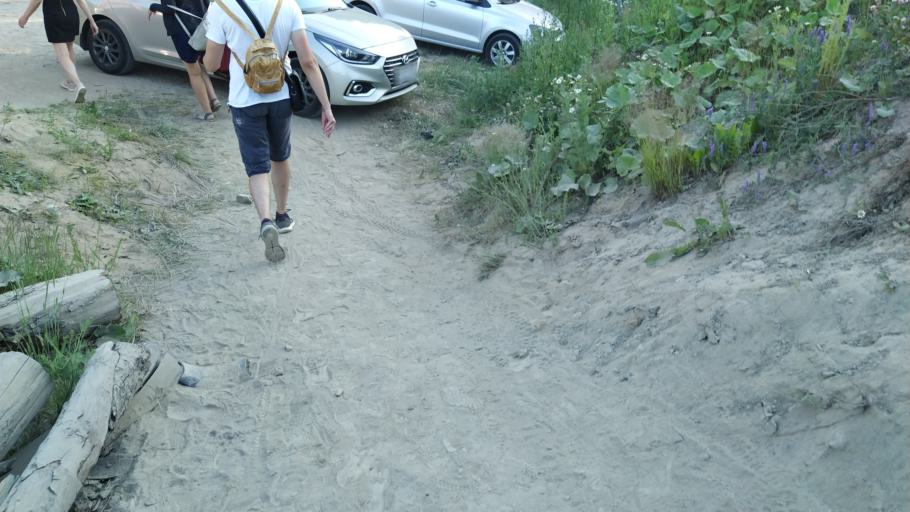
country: RU
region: Leningrad
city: Toksovo
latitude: 60.1137
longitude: 30.5192
